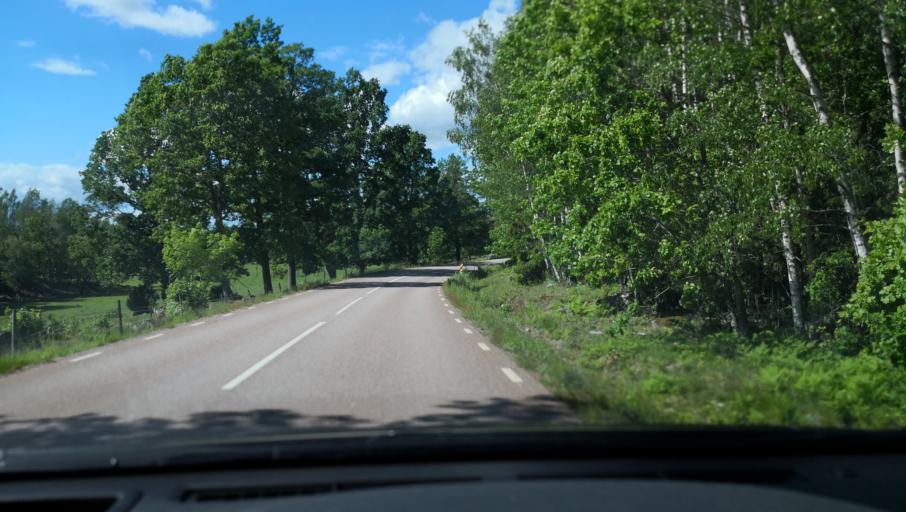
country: SE
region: Vaestmanland
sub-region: Arboga Kommun
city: Tyringe
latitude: 59.3004
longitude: 16.0200
